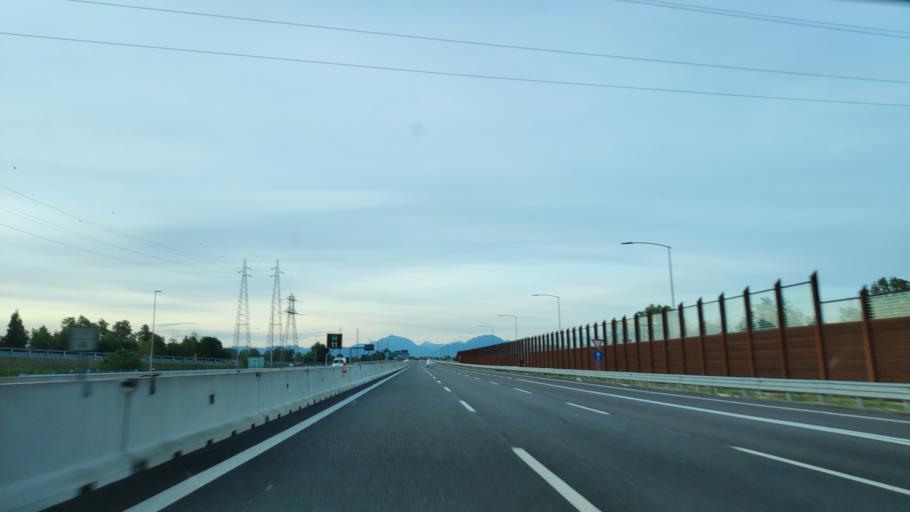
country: IT
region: Lombardy
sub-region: Citta metropolitana di Milano
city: Pozzuolo Martesana
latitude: 45.5176
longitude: 9.4402
